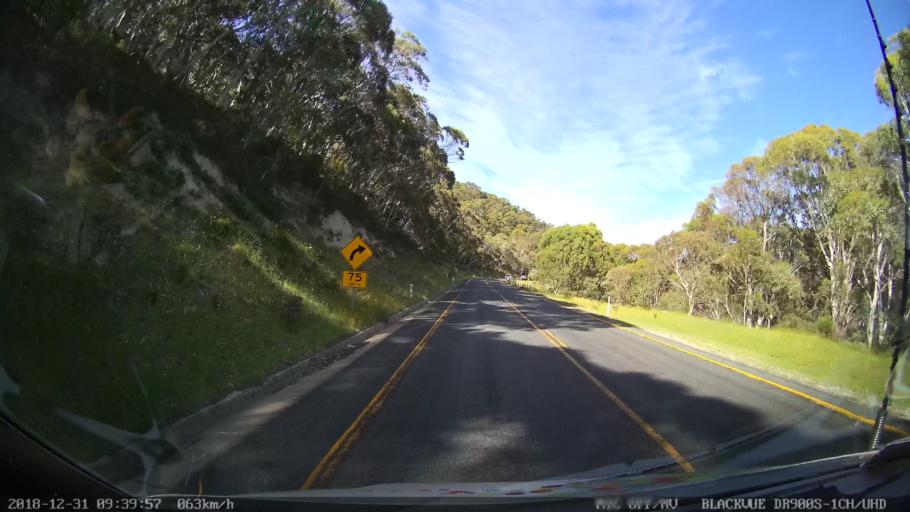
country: AU
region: New South Wales
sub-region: Snowy River
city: Jindabyne
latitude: -36.4816
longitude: 148.3495
